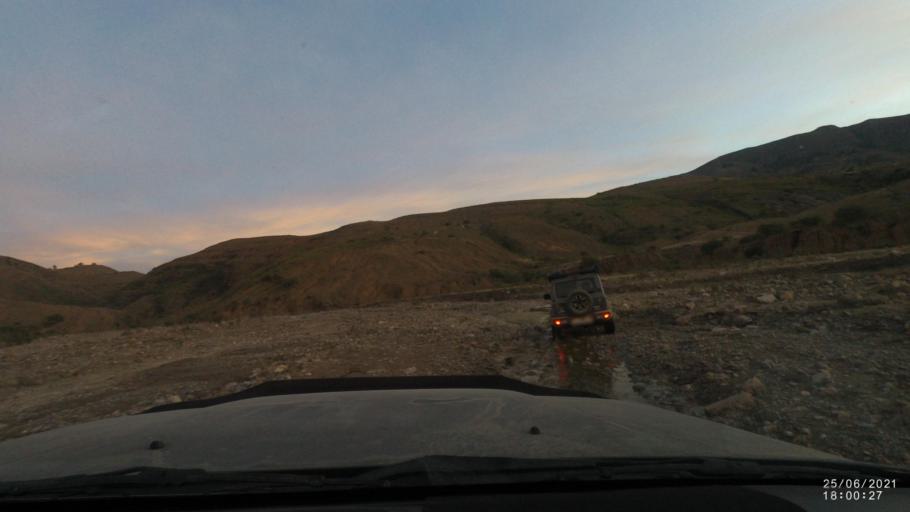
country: BO
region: Cochabamba
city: Mizque
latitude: -17.9458
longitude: -65.6350
